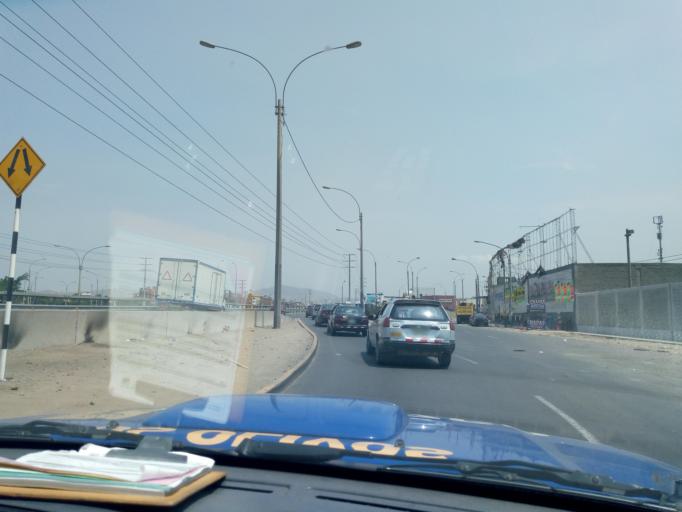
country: PE
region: Lima
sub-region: Lima
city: Independencia
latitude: -11.9797
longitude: -77.0653
